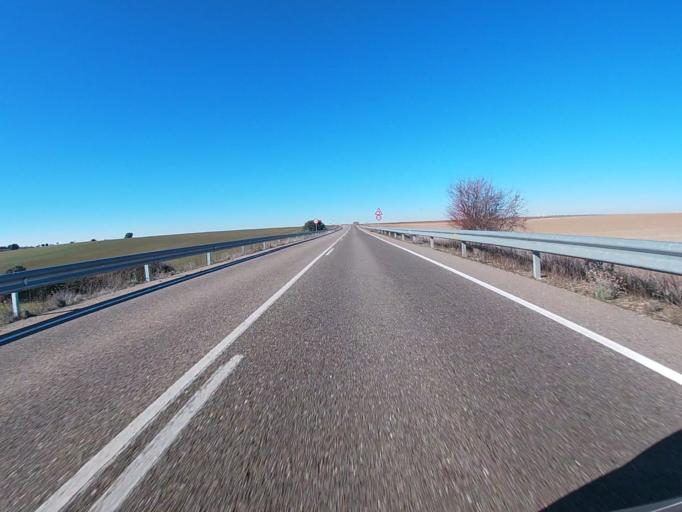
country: ES
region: Castille and Leon
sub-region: Provincia de Salamanca
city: Almenara de Tormes
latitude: 41.0733
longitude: -5.8328
